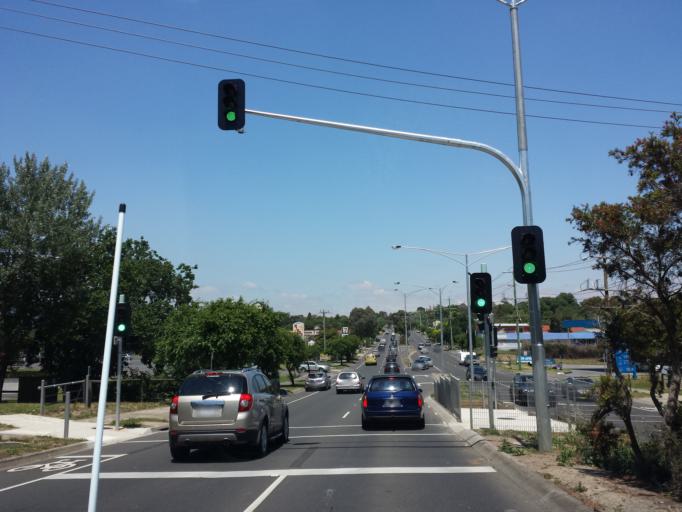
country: AU
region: Victoria
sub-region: Maroondah
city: Croydon North
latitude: -37.8022
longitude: 145.2894
